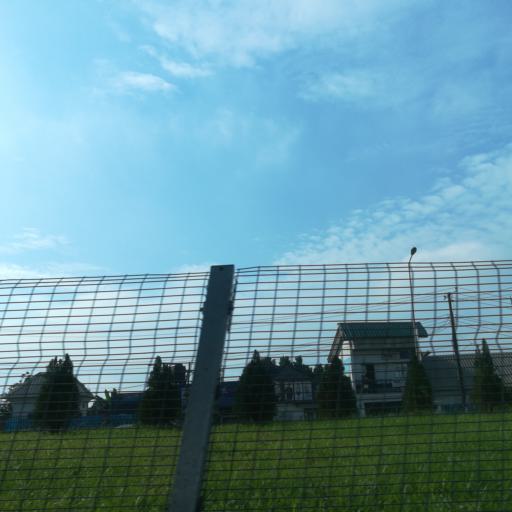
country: NG
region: Rivers
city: Port Harcourt
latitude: 4.8096
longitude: 7.0176
